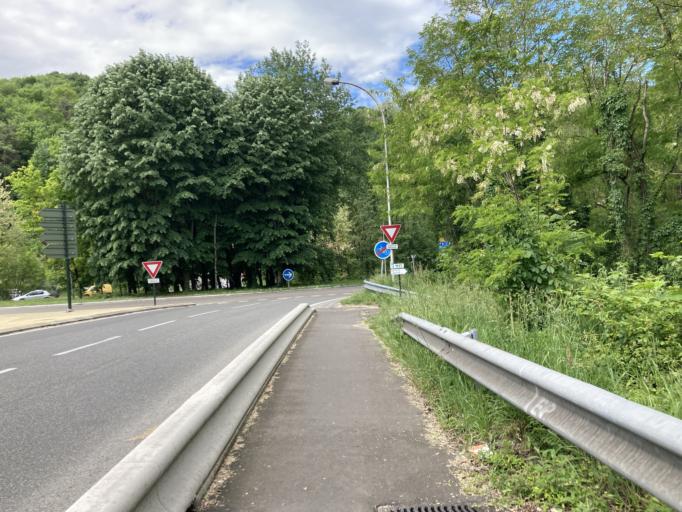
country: FR
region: Aquitaine
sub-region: Departement des Pyrenees-Atlantiques
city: Billere
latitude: 43.2964
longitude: -0.4144
